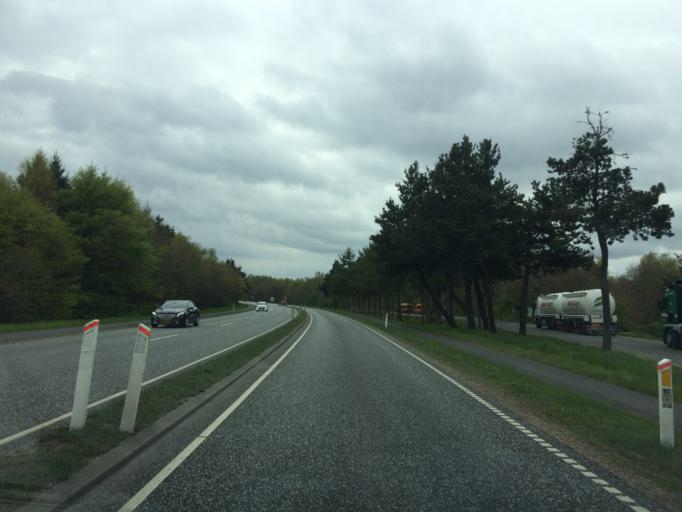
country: DK
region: Central Jutland
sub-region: Viborg Kommune
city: Viborg
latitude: 56.4075
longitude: 9.3716
